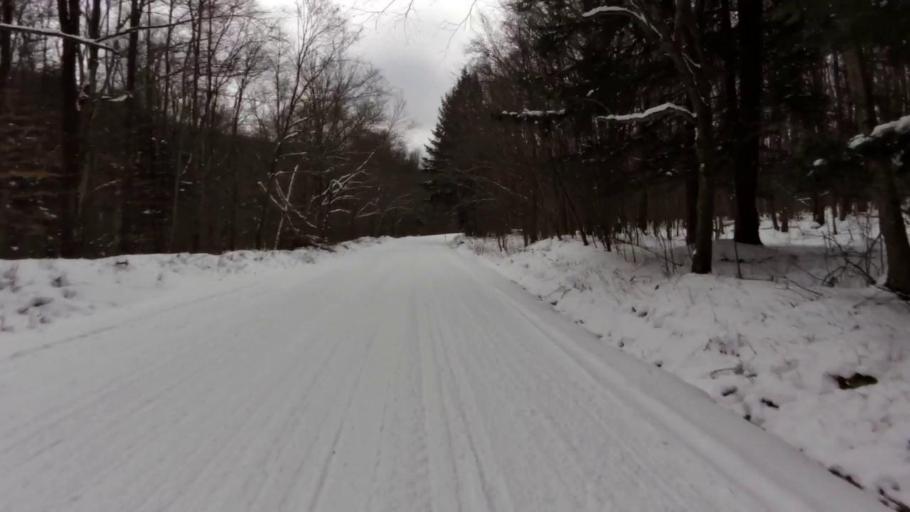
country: US
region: New York
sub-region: Cattaraugus County
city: Salamanca
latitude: 42.0235
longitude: -78.8156
